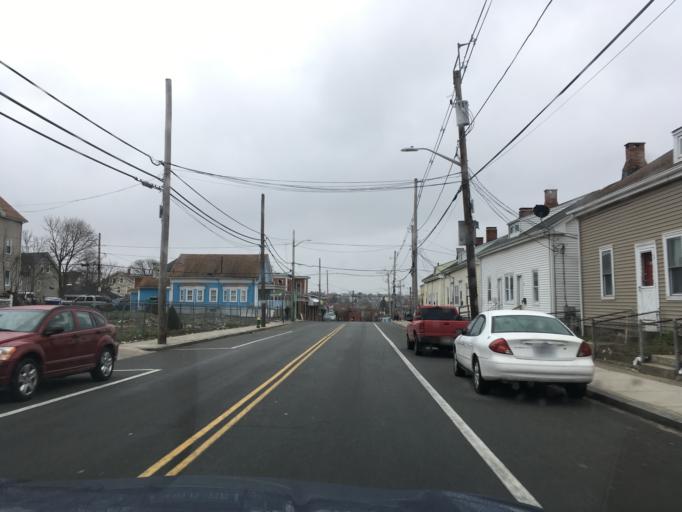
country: US
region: Rhode Island
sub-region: Providence County
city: North Providence
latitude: 41.8207
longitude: -71.4476
